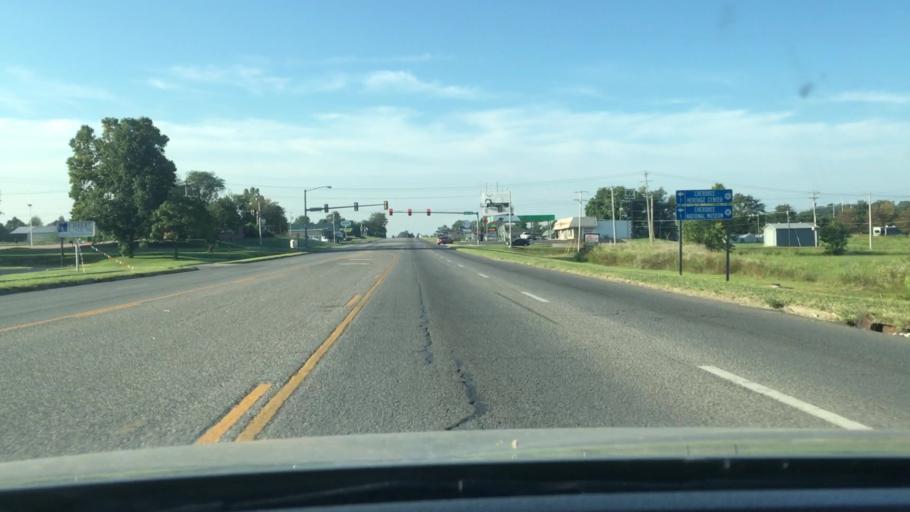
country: US
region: Oklahoma
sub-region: Cherokee County
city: Park Hill
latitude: 35.8722
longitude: -94.9763
